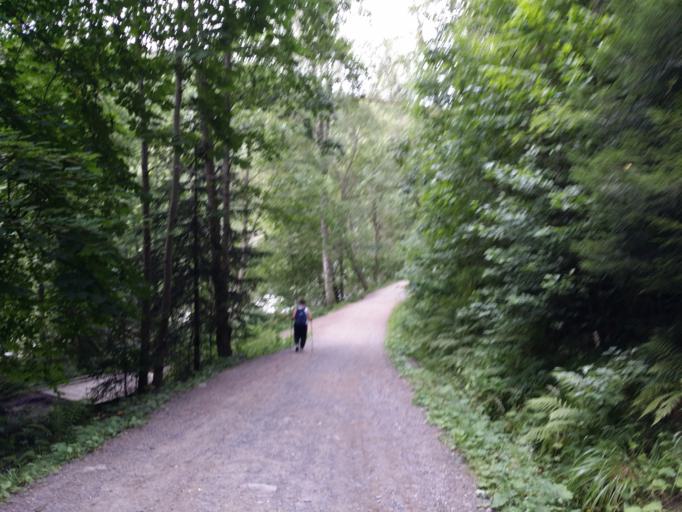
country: NO
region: Akershus
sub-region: Lorenskog
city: Kjenn
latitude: 59.8934
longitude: 10.8776
